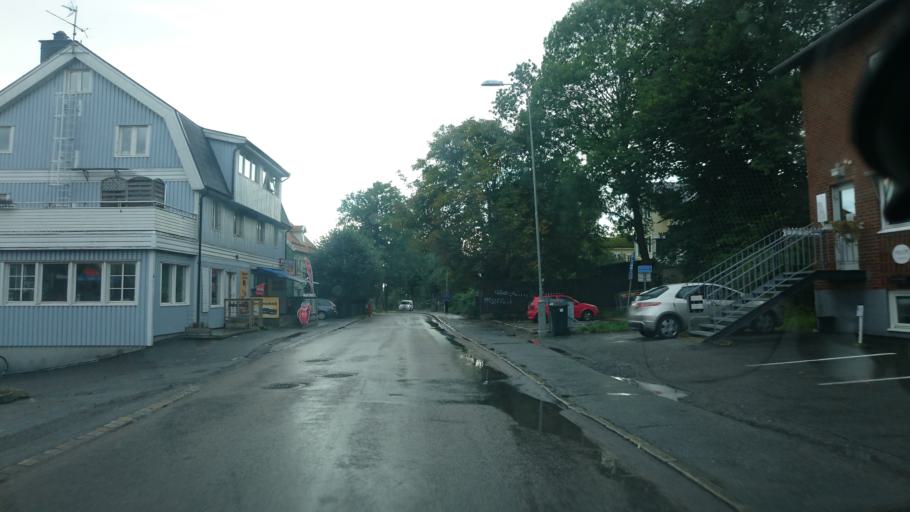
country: SE
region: Vaestra Goetaland
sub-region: Goteborg
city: Majorna
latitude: 57.6796
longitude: 11.8978
